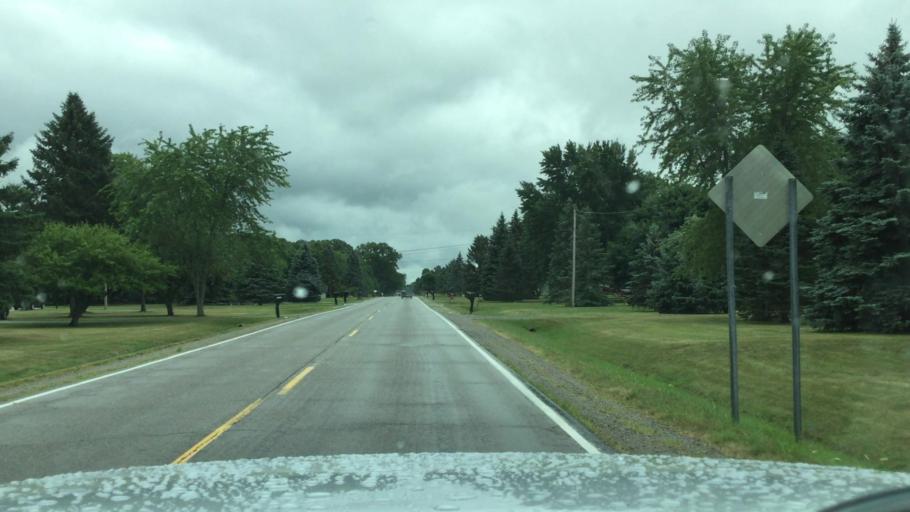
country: US
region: Michigan
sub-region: Genesee County
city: Clio
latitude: 43.1317
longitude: -83.7738
